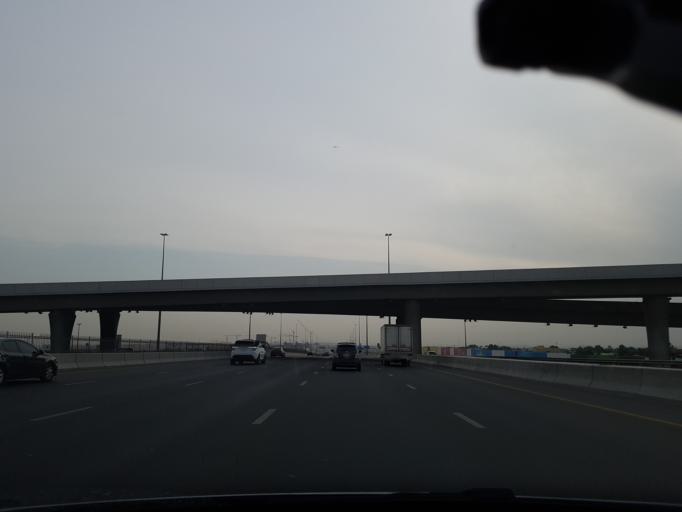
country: AE
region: Ash Shariqah
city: Sharjah
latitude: 25.3345
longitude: 55.4654
